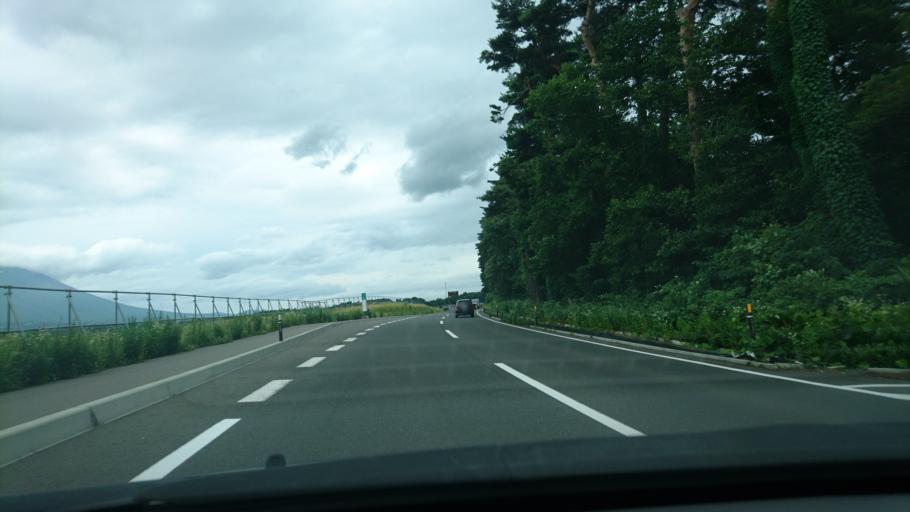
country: JP
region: Iwate
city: Morioka-shi
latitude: 39.7756
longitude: 141.1267
